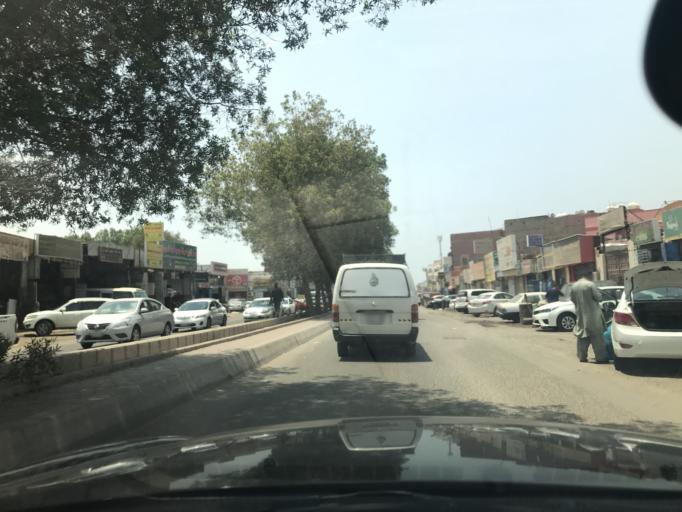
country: SA
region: Makkah
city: Jeddah
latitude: 21.4608
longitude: 39.2293
